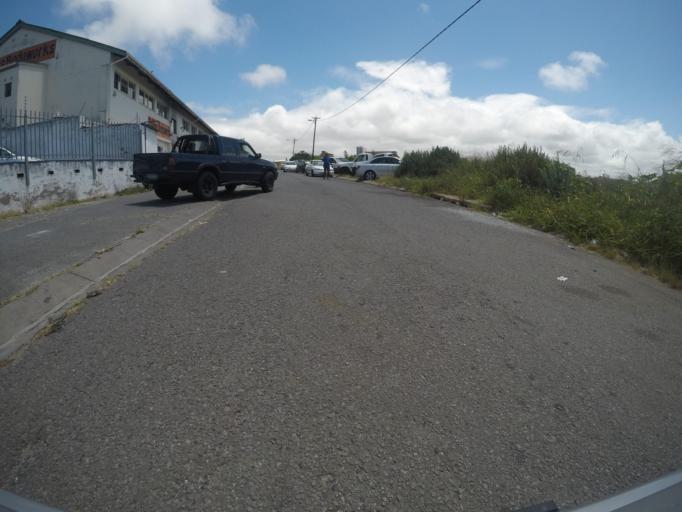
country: ZA
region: Eastern Cape
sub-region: Buffalo City Metropolitan Municipality
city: East London
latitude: -33.0060
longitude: 27.9122
